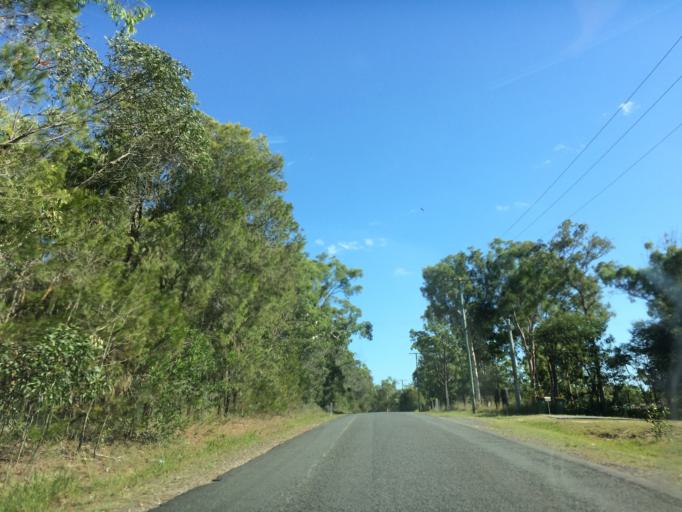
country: AU
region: Queensland
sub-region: Ipswich
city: Springfield Lakes
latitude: -27.7065
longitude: 152.9567
